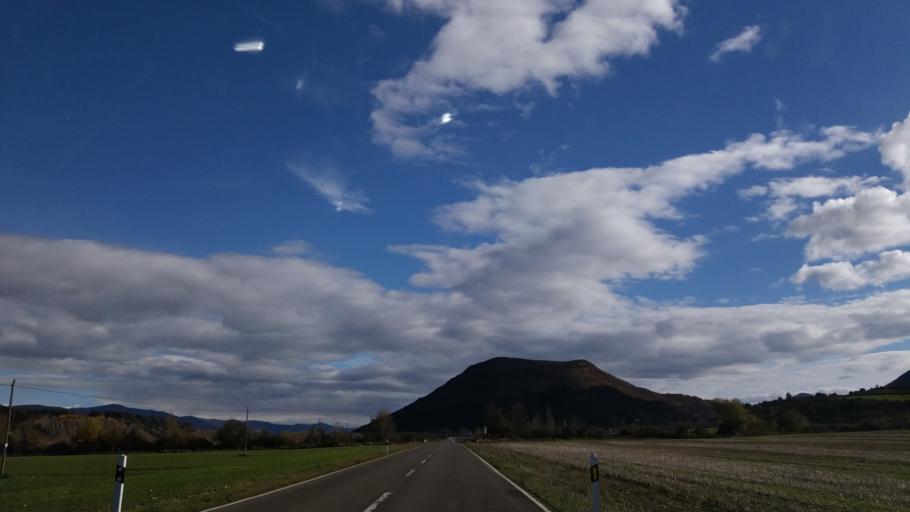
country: ES
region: Aragon
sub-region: Provincia de Huesca
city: Santa Cruz de la Seros
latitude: 42.5563
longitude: -0.6933
